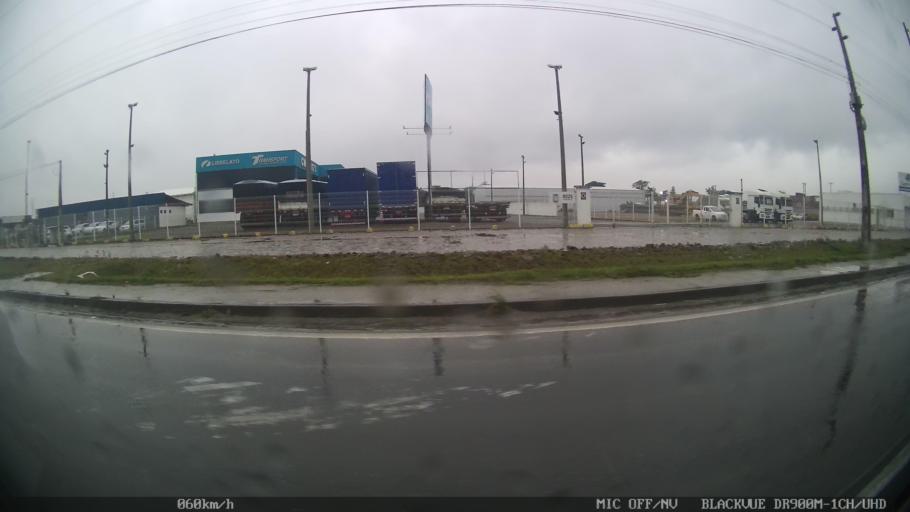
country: BR
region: Santa Catarina
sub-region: Itajai
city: Itajai
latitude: -26.9127
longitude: -48.7116
